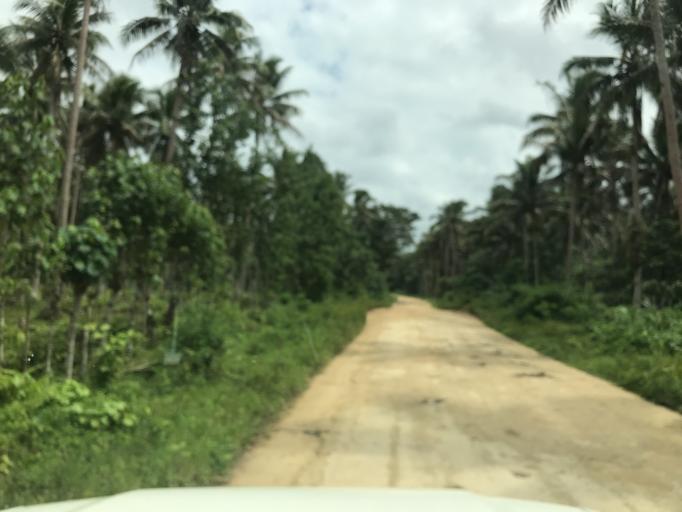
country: VU
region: Sanma
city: Port-Olry
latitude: -15.1766
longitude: 167.0948
